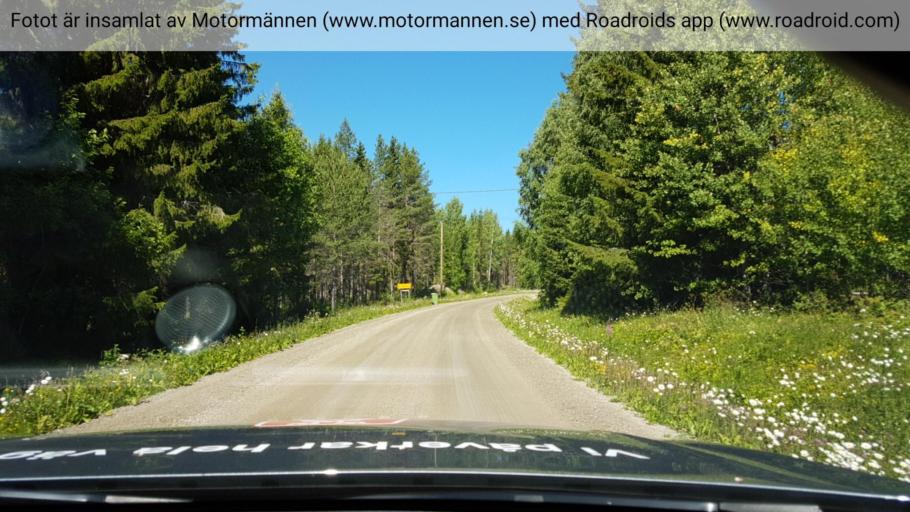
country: SE
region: Jaemtland
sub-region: Braecke Kommun
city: Braecke
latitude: 62.8040
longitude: 15.2275
